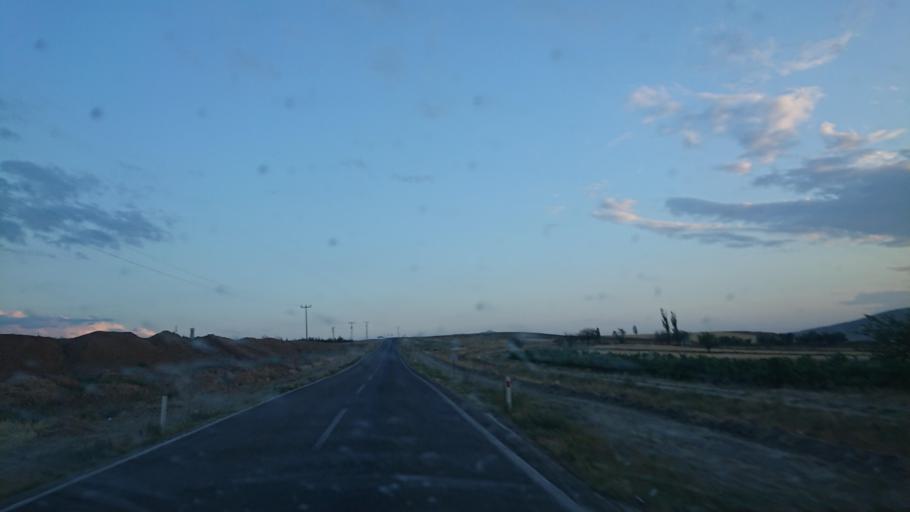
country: TR
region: Aksaray
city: Balci
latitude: 38.8037
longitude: 34.1304
